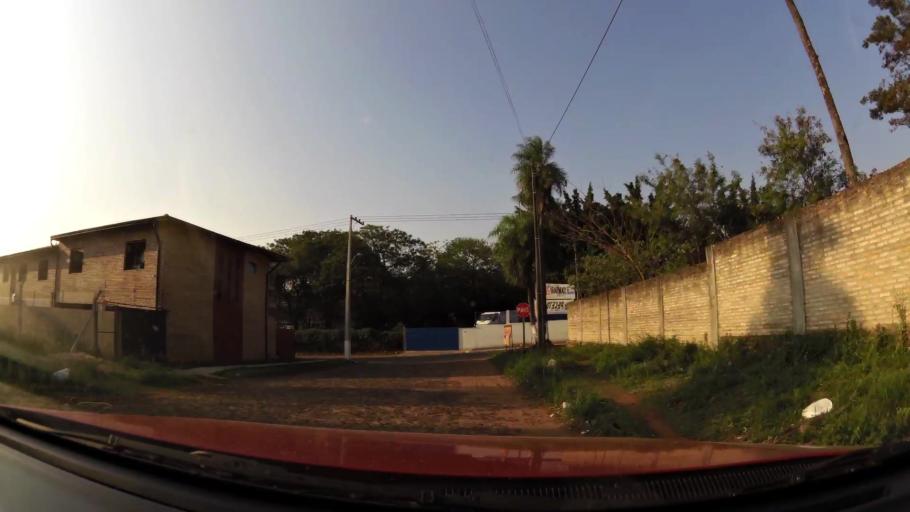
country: PY
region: Central
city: Lambare
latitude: -25.3568
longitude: -57.6013
